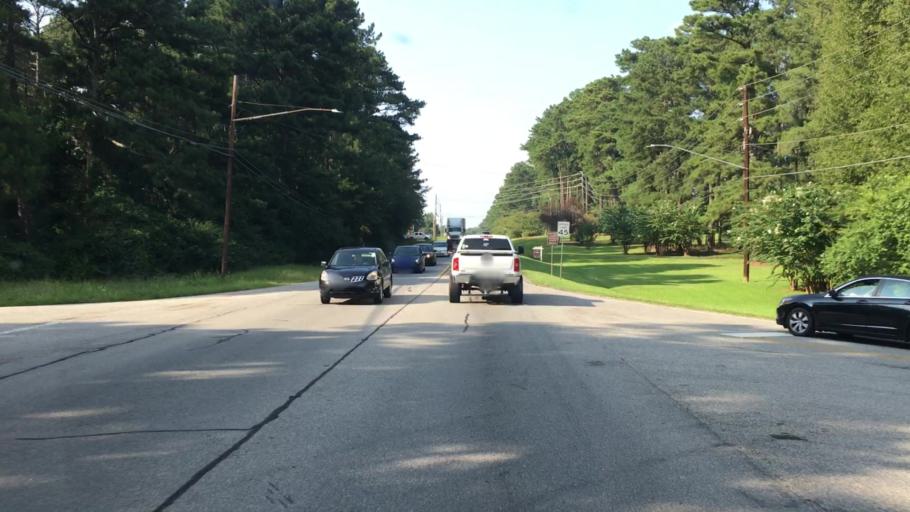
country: US
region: Georgia
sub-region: Barrow County
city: Russell
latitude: 33.9754
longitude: -83.7132
